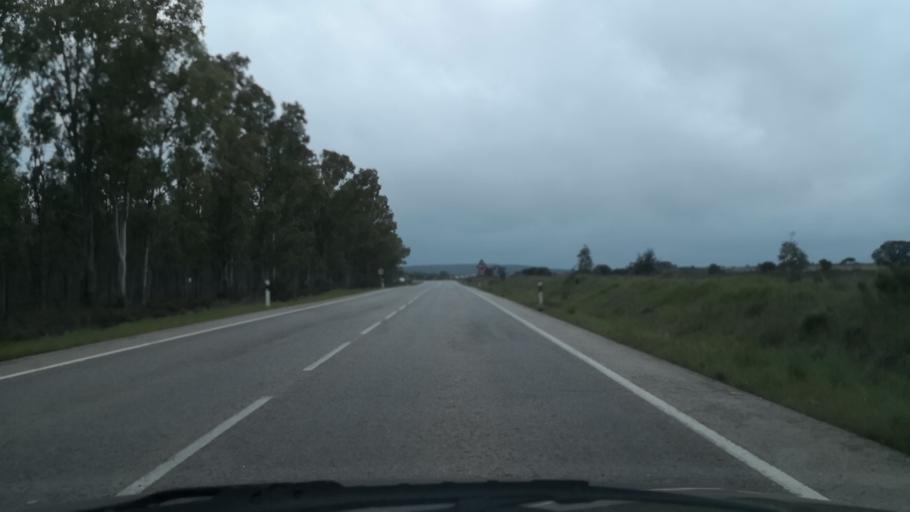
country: ES
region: Extremadura
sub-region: Provincia de Caceres
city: Malpartida de Caceres
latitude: 39.3279
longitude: -6.4920
